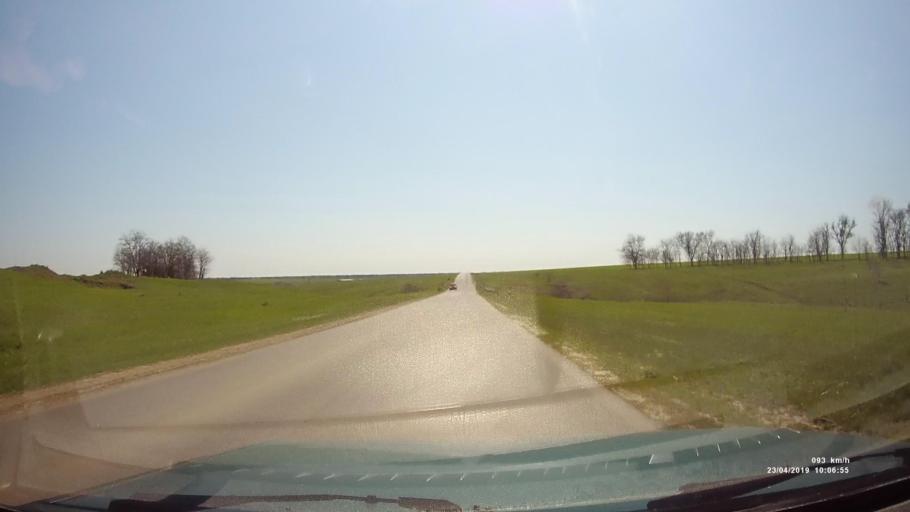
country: RU
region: Rostov
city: Sovetskoye
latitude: 46.7292
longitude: 42.2454
